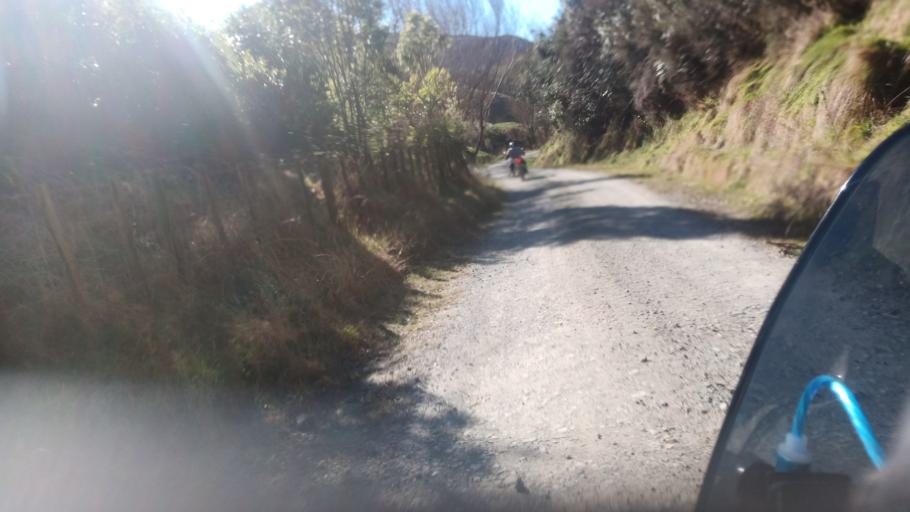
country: NZ
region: Hawke's Bay
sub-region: Wairoa District
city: Wairoa
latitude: -38.6604
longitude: 177.4886
